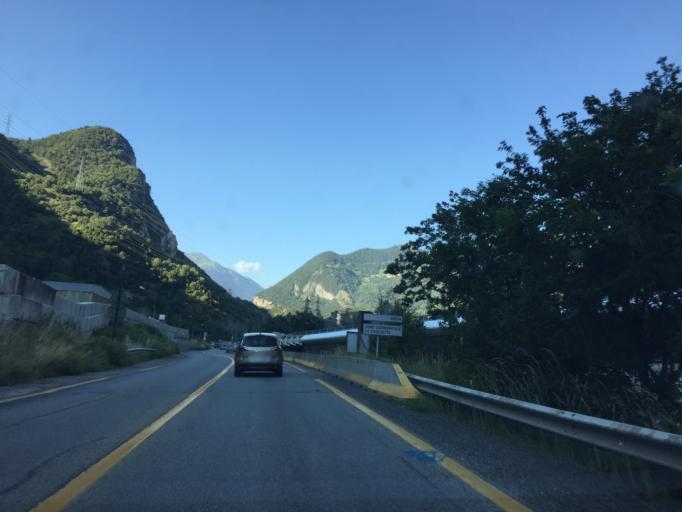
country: FR
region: Rhone-Alpes
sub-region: Departement de la Savoie
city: Moutiers
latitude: 45.4912
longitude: 6.5498
